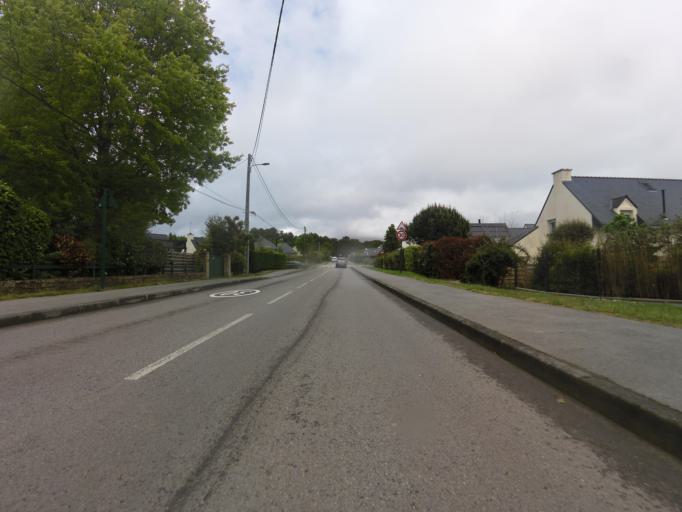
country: FR
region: Brittany
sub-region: Departement du Morbihan
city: Baden
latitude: 47.6237
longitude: -2.9232
